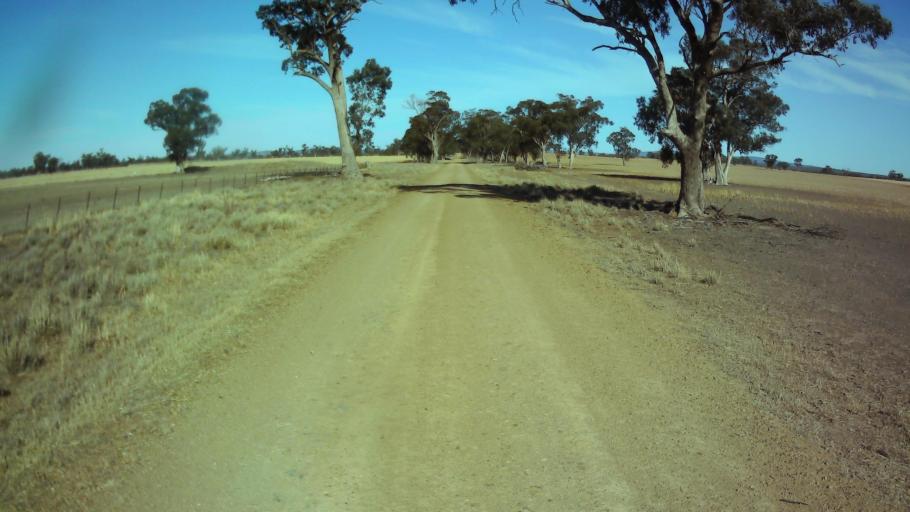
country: AU
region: New South Wales
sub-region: Weddin
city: Grenfell
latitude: -33.6598
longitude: 148.1117
